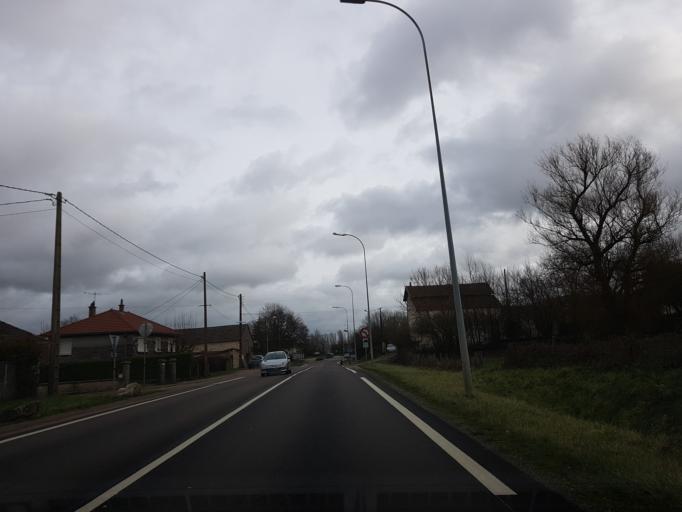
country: FR
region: Champagne-Ardenne
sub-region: Departement de la Haute-Marne
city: Langres
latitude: 47.8720
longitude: 5.3358
